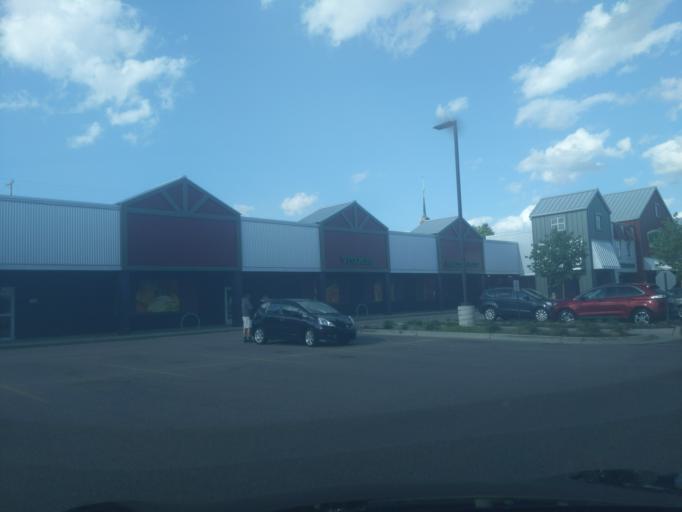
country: US
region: Michigan
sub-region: Ingham County
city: East Lansing
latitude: 42.7204
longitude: -84.4958
